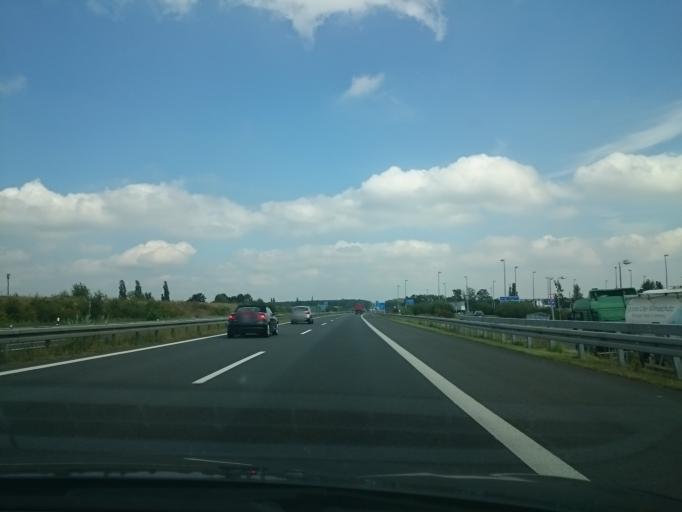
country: DE
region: Brandenburg
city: Joachimsthal
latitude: 52.8835
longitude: 13.7039
